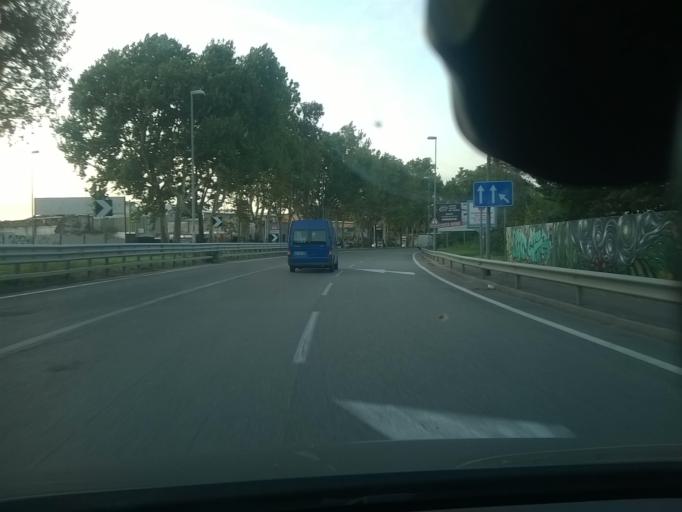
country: IT
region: Lombardy
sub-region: Provincia di Bergamo
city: Gorle
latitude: 45.7009
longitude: 9.6961
